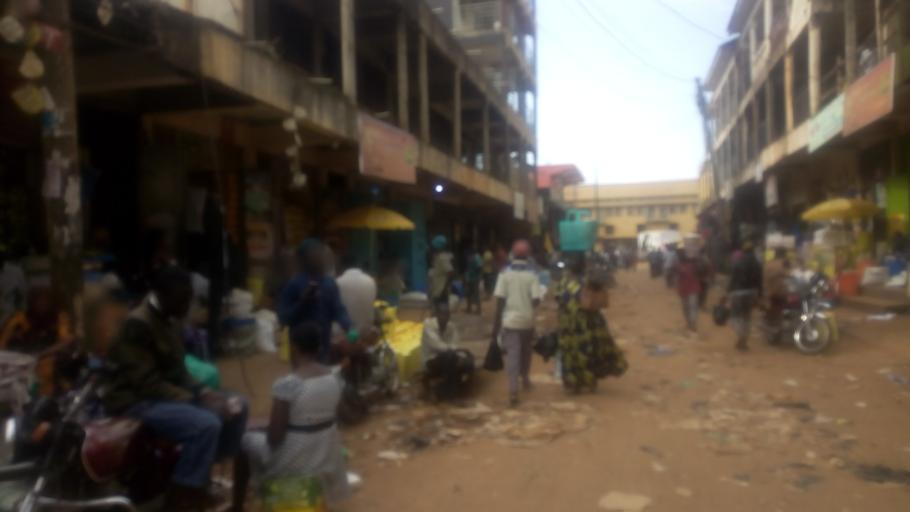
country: UG
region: Eastern Region
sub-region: Mbale District
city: Mbale
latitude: 1.0710
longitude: 34.1775
